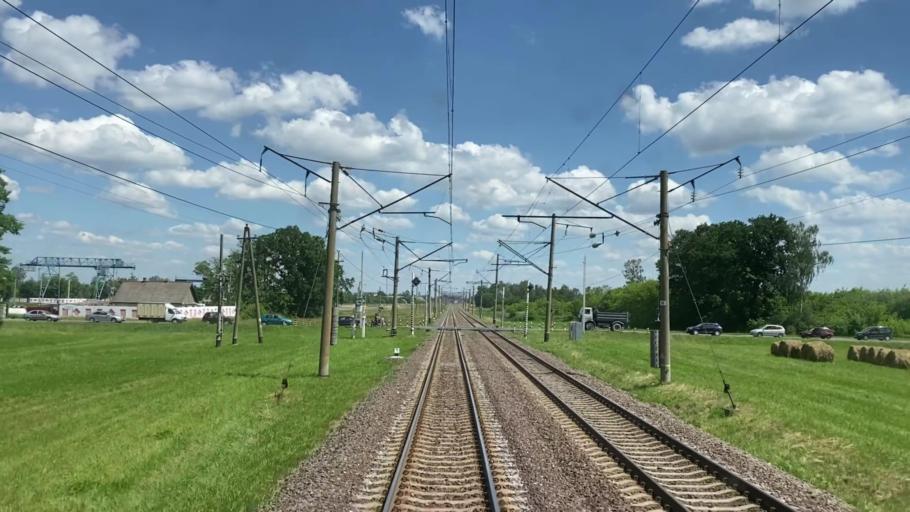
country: BY
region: Brest
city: Ivatsevichy
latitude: 52.6973
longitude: 25.3177
